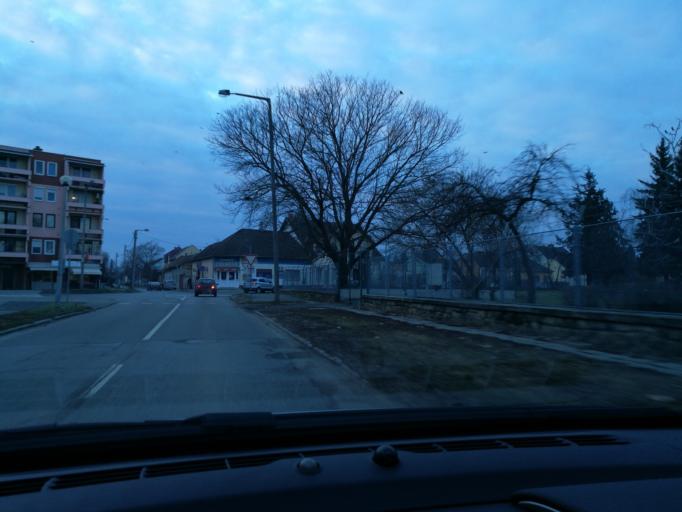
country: HU
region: Szabolcs-Szatmar-Bereg
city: Nyiregyhaza
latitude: 47.9690
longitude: 21.7095
